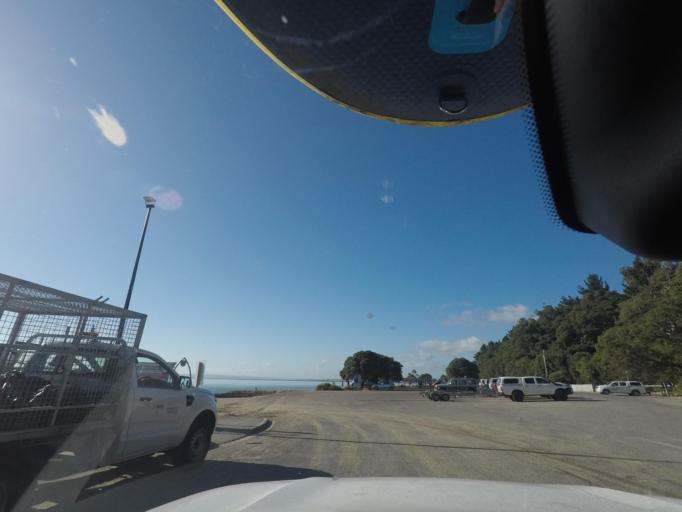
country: NZ
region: Auckland
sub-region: Auckland
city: Parakai
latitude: -36.5707
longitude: 174.3789
